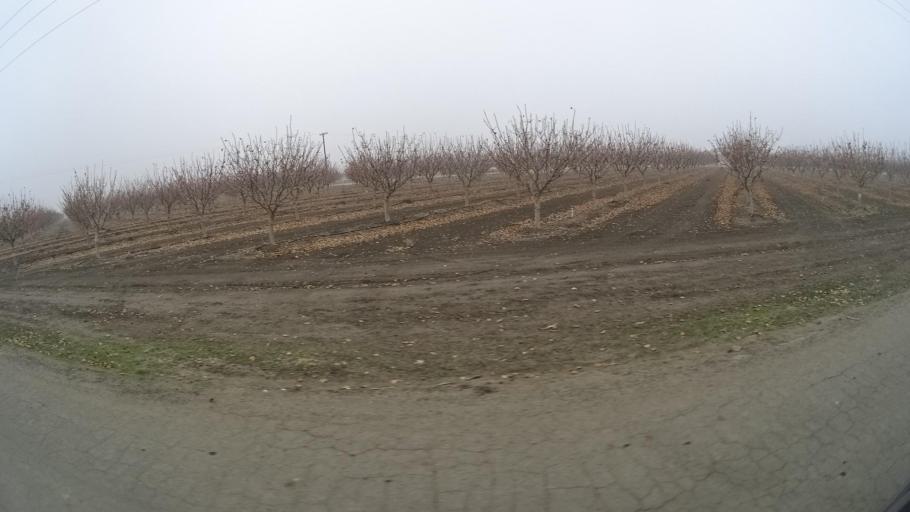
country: US
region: California
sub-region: Kern County
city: Buttonwillow
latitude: 35.4559
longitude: -119.5184
